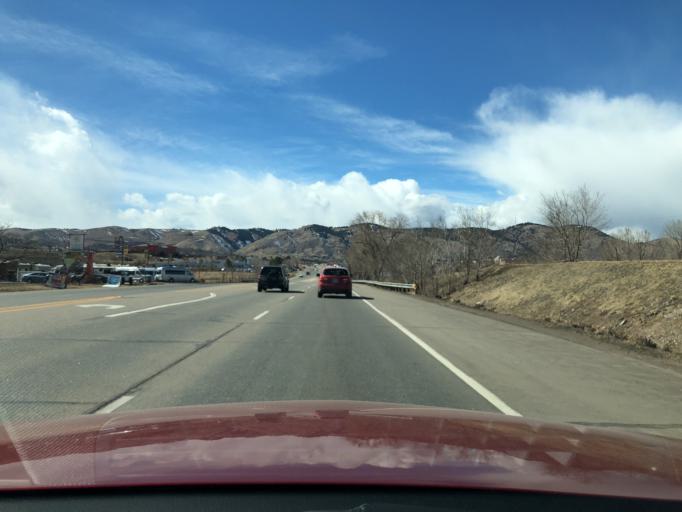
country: US
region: Colorado
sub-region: Jefferson County
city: West Pleasant View
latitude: 39.7290
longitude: -105.1779
